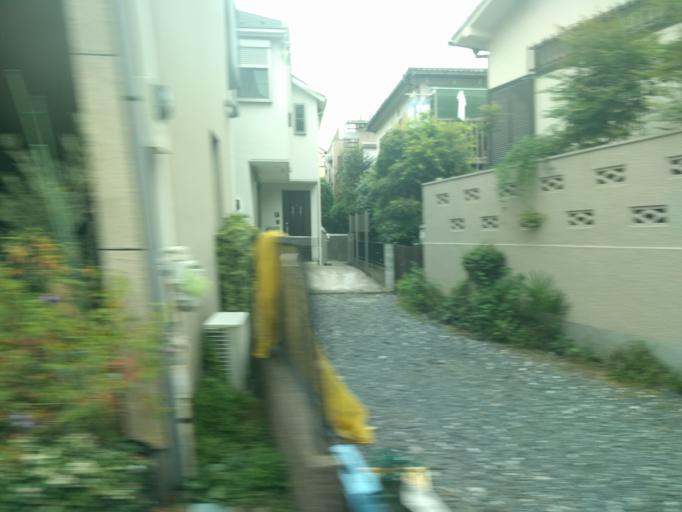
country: JP
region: Tokyo
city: Tokyo
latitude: 35.6342
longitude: 139.6962
